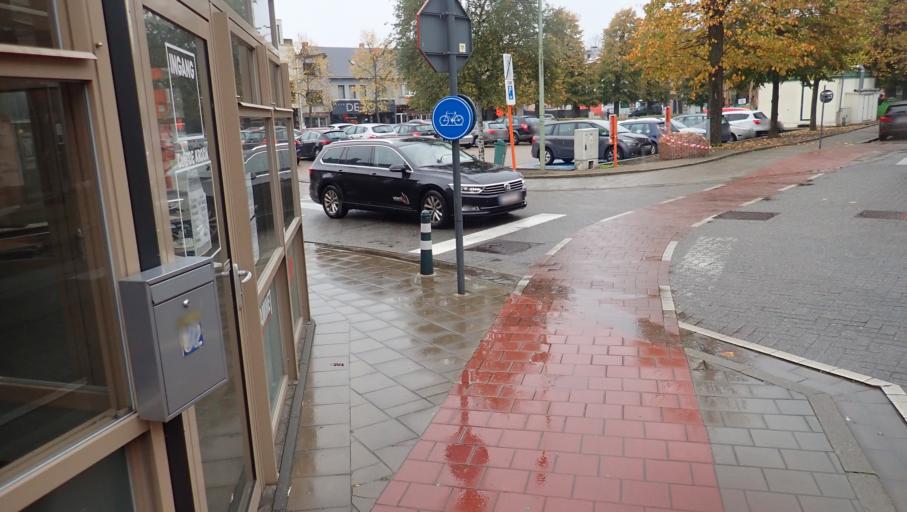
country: BE
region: Flanders
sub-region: Provincie Antwerpen
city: Berlaar
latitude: 51.1173
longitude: 4.6566
